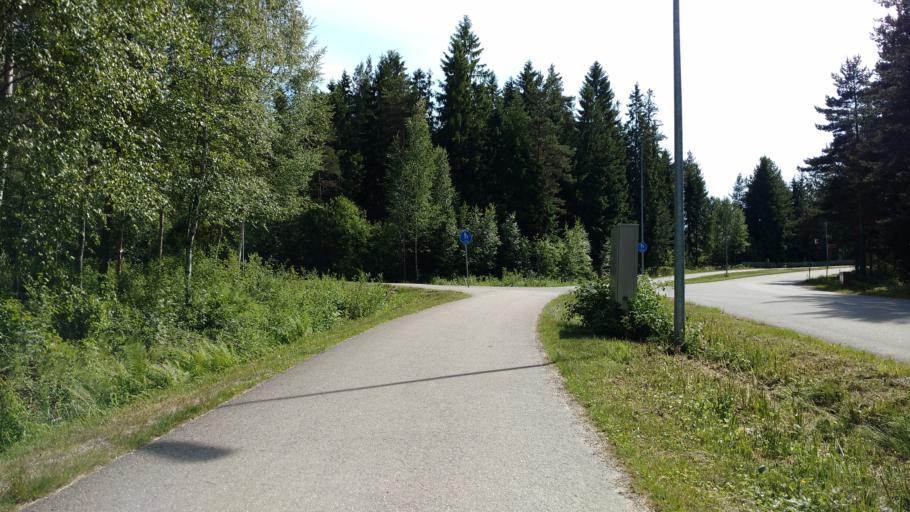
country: FI
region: Varsinais-Suomi
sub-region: Salo
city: Salo
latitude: 60.4060
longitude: 23.1923
